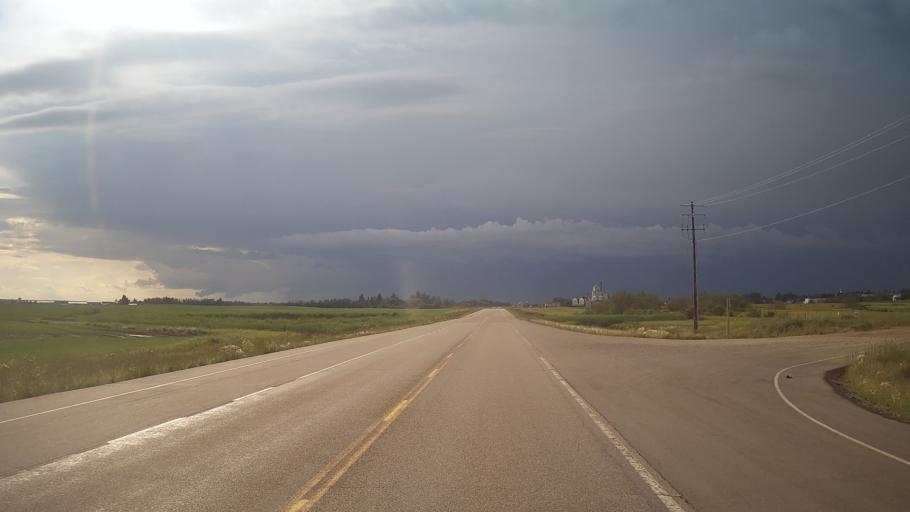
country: CA
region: Alberta
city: Vegreville
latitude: 53.2248
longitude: -112.2277
